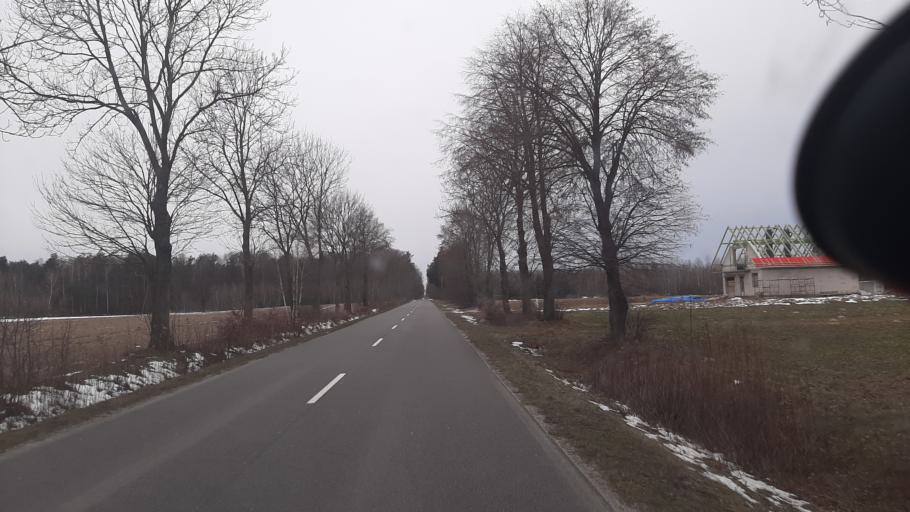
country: PL
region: Lublin Voivodeship
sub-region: Powiat lubartowski
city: Kamionka
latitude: 51.4959
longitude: 22.4185
